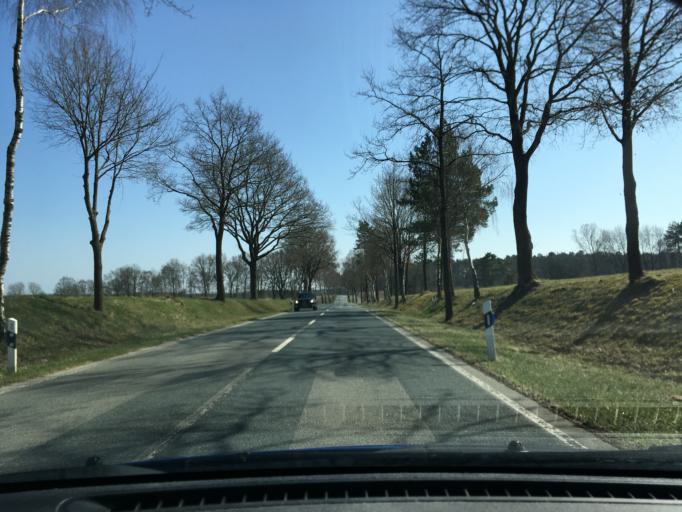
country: DE
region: Lower Saxony
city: Wriedel
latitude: 53.0828
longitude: 10.2762
